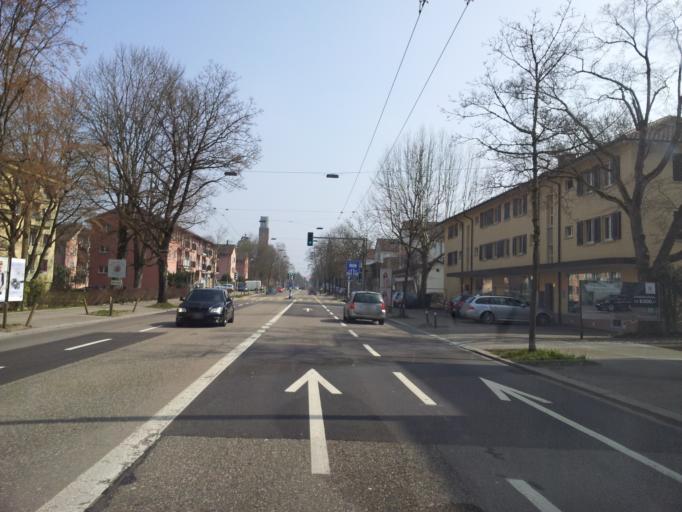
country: CH
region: Zurich
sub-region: Bezirk Zuerich
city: Zuerich (Kreis 11) / Affoltern
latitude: 47.4153
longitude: 8.5143
